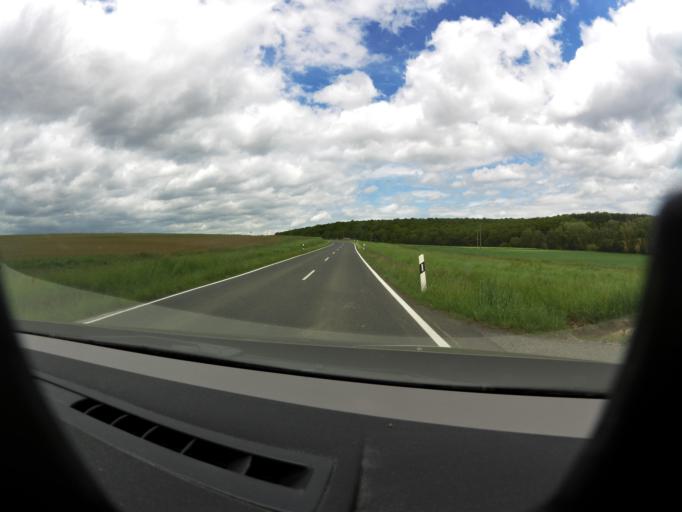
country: DE
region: Bavaria
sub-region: Regierungsbezirk Unterfranken
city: Prosselsheim
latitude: 49.8448
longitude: 10.1448
